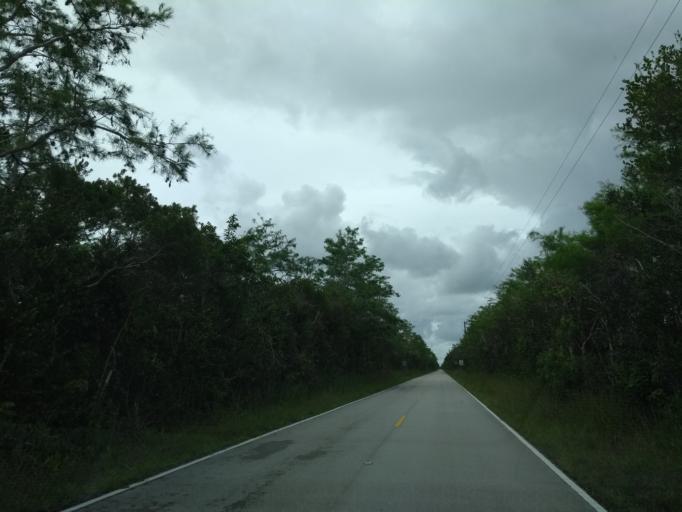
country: US
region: Florida
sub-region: Miami-Dade County
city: The Hammocks
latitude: 25.7613
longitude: -80.8937
